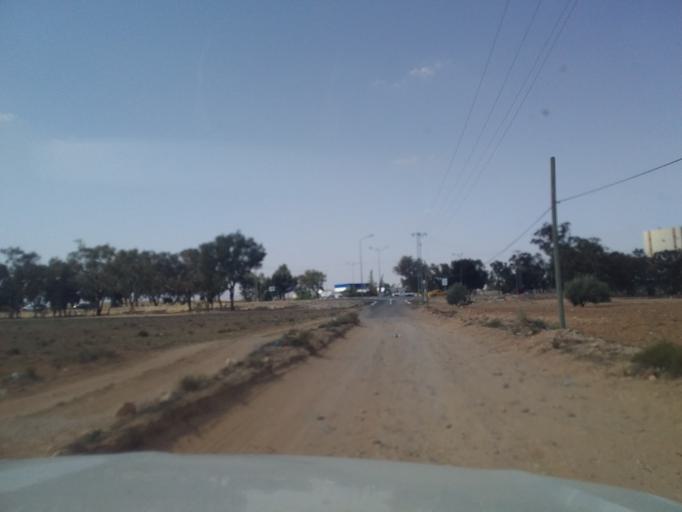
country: TN
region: Madanin
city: Medenine
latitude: 33.5995
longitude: 10.3109
